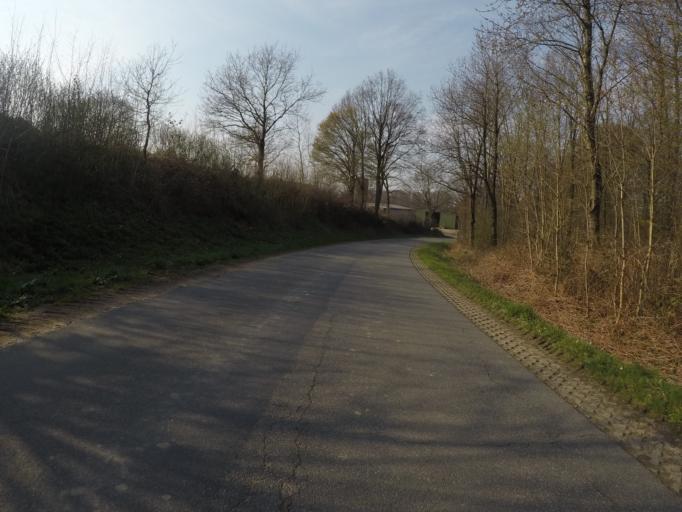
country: DE
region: Schleswig-Holstein
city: Kukels
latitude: 53.8868
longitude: 10.2408
